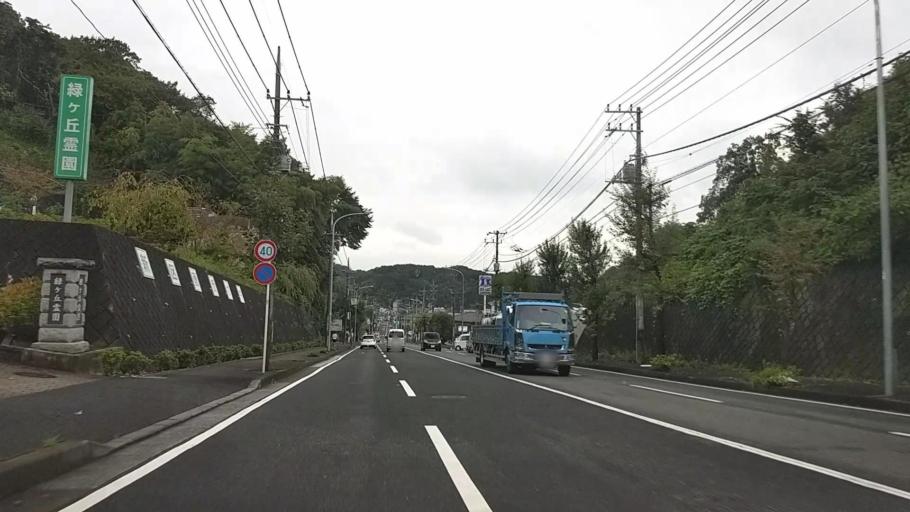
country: JP
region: Kanagawa
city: Kamakura
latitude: 35.4012
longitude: 139.5561
